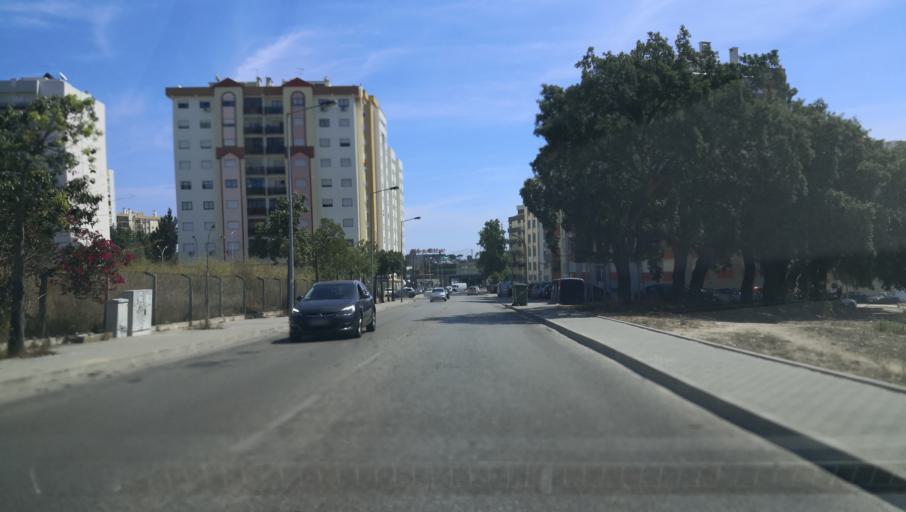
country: PT
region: Setubal
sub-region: Setubal
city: Setubal
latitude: 38.5333
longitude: -8.8708
